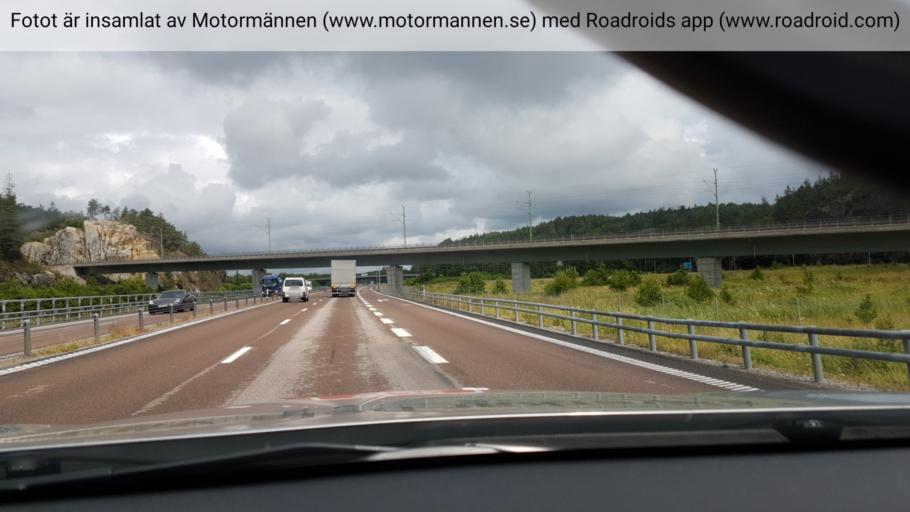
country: SE
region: Vaestra Goetaland
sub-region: Stromstads Kommun
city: Stroemstad
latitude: 58.9289
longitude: 11.2555
